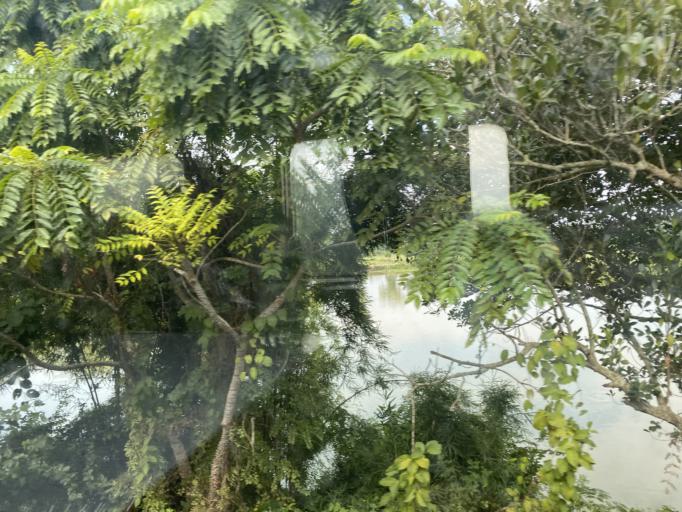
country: IN
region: Tripura
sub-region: West Tripura
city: Agartala
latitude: 24.0010
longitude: 91.2943
